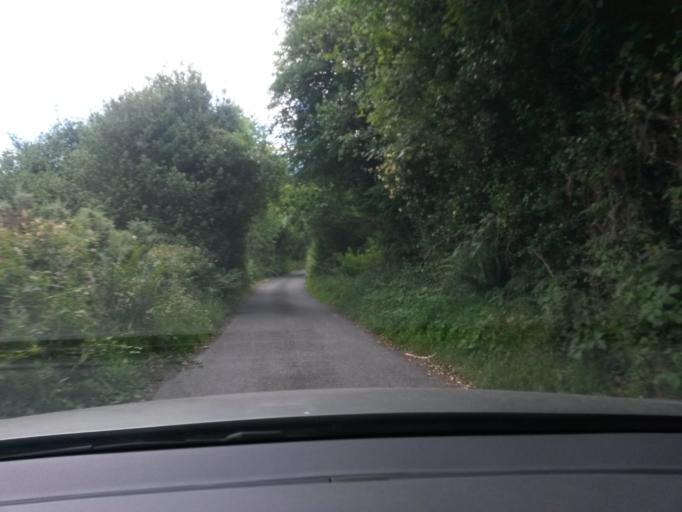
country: IE
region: Leinster
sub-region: Wicklow
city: Enniskerry
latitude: 53.1681
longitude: -6.2326
